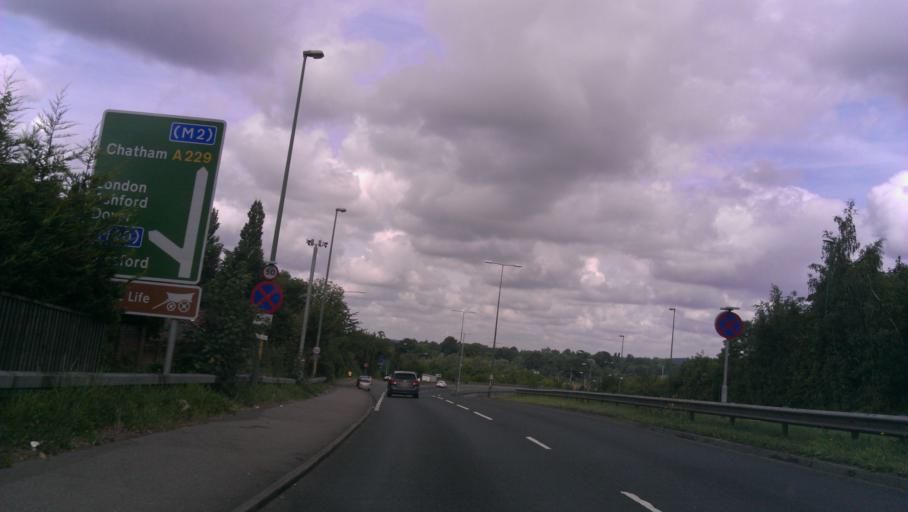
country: GB
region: England
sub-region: Kent
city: Maidstone
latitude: 51.2931
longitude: 0.5167
